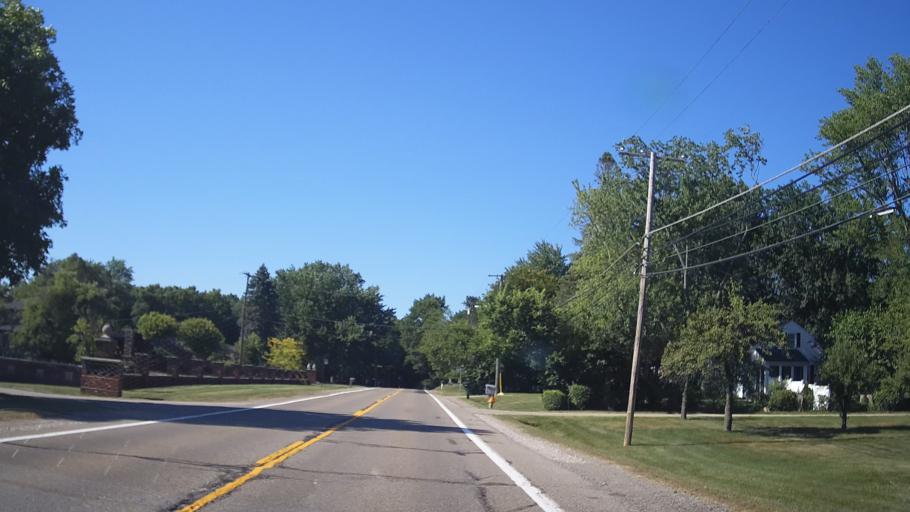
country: US
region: Michigan
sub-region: Macomb County
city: Clinton
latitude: 42.5912
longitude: -82.9137
